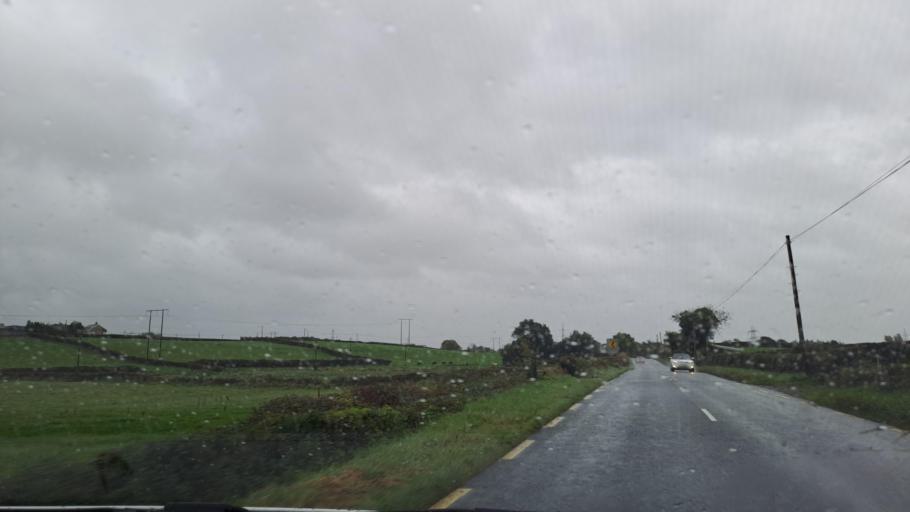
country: GB
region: Northern Ireland
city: Crossmaglen
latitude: 53.9703
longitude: -6.5801
